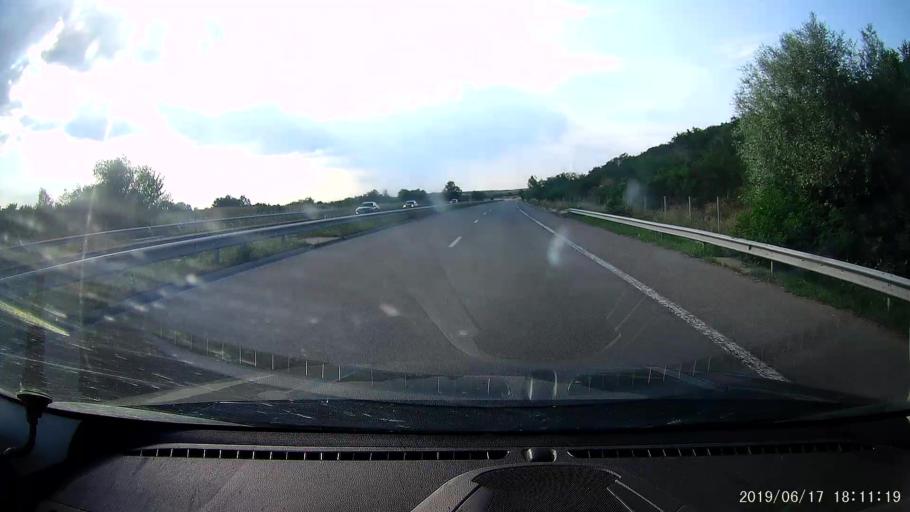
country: BG
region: Khaskovo
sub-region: Obshtina Lyubimets
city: Lyubimets
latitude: 41.8822
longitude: 26.0535
